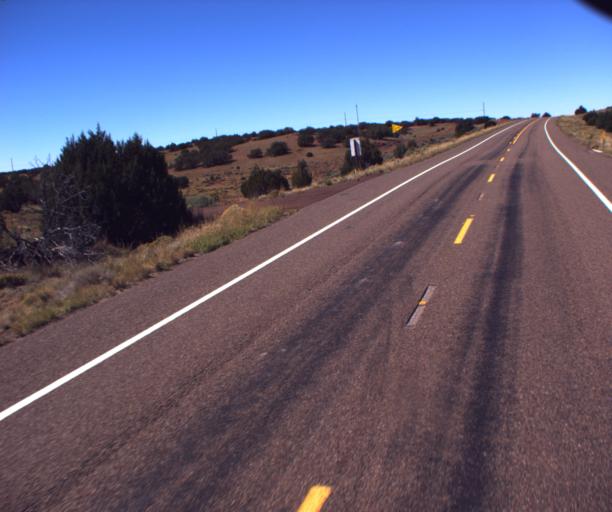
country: US
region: Arizona
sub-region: Apache County
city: Saint Johns
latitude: 34.5975
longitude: -109.6318
